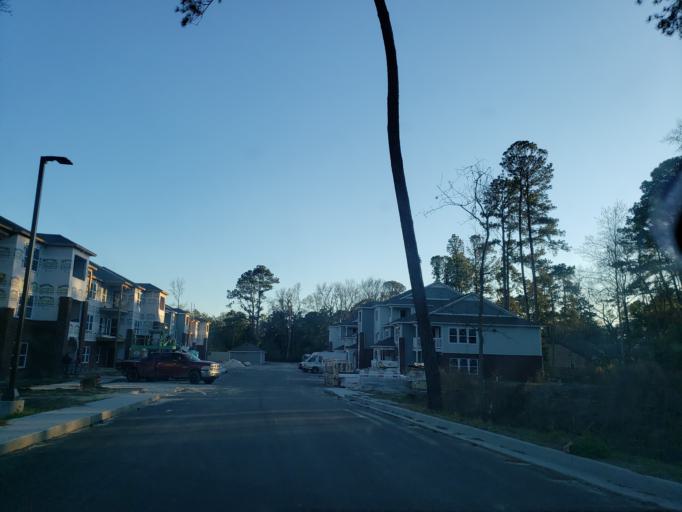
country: US
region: Georgia
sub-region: Chatham County
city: Montgomery
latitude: 31.9978
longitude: -81.1356
